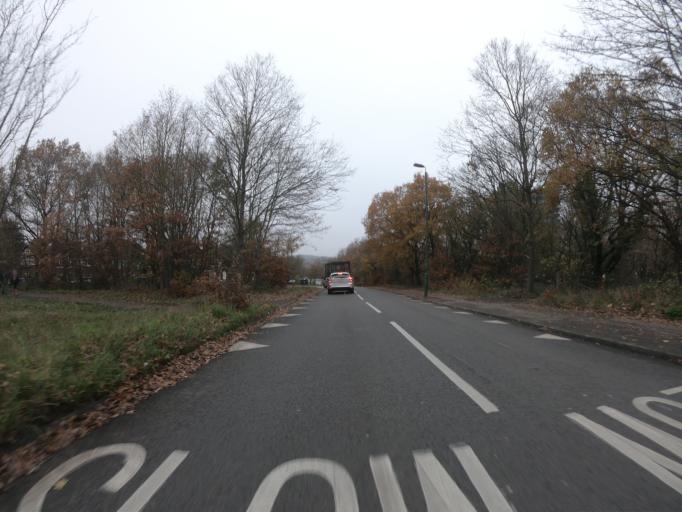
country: GB
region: England
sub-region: Greater London
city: Woodford Green
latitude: 51.6036
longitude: 0.0095
